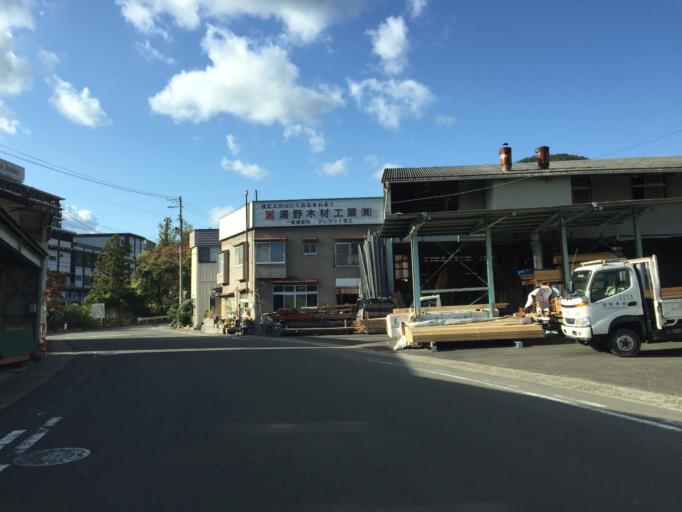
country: JP
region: Fukushima
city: Fukushima-shi
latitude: 37.8344
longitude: 140.4542
